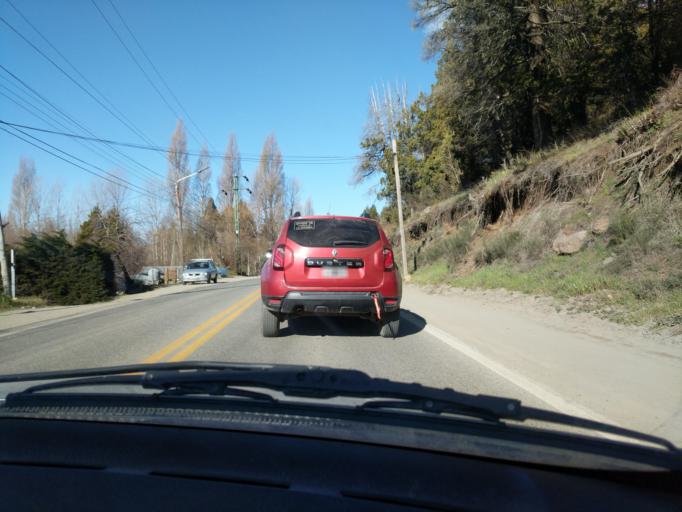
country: AR
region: Rio Negro
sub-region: Departamento de Bariloche
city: San Carlos de Bariloche
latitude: -41.1263
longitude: -71.3850
